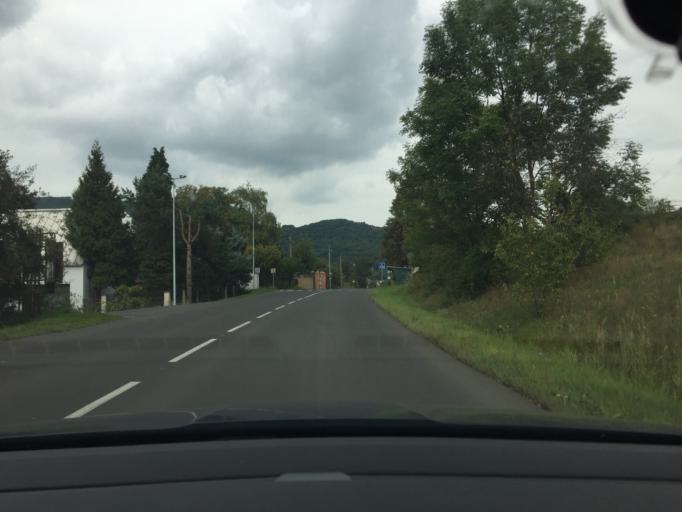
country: CZ
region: Ustecky
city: Trmice
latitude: 50.5889
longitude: 14.0359
